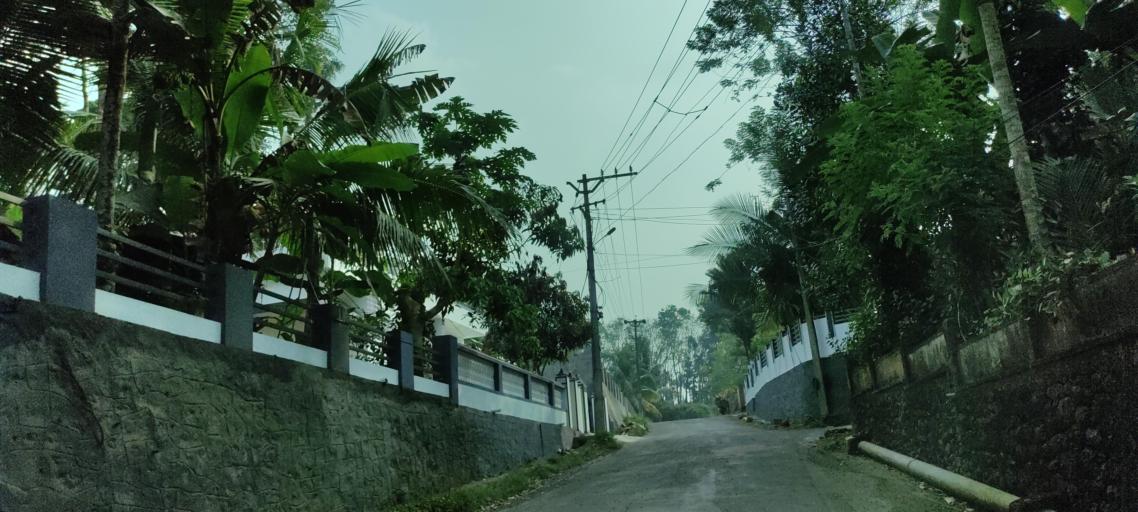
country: IN
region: Kerala
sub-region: Ernakulam
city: Piravam
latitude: 9.7989
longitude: 76.5354
